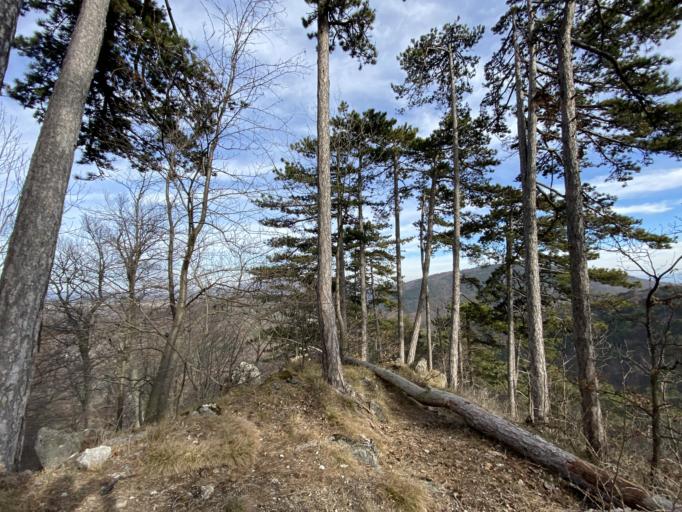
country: AT
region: Lower Austria
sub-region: Politischer Bezirk Baden
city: Heiligenkreuz
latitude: 48.0101
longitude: 16.1592
